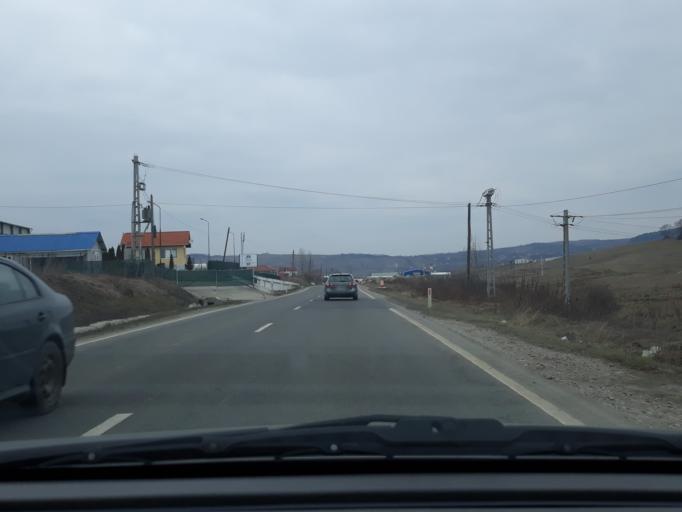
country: RO
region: Salaj
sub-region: Comuna Hereclean
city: Hereclean
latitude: 47.2327
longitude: 22.9778
